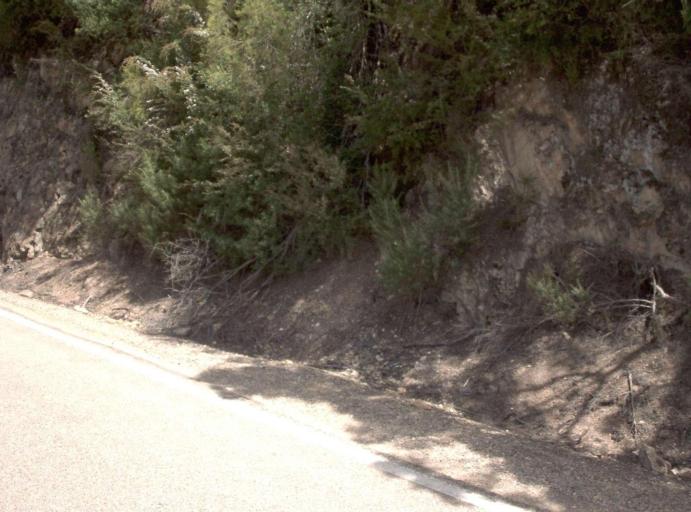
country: AU
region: Victoria
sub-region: East Gippsland
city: Lakes Entrance
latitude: -37.5569
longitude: 147.8865
